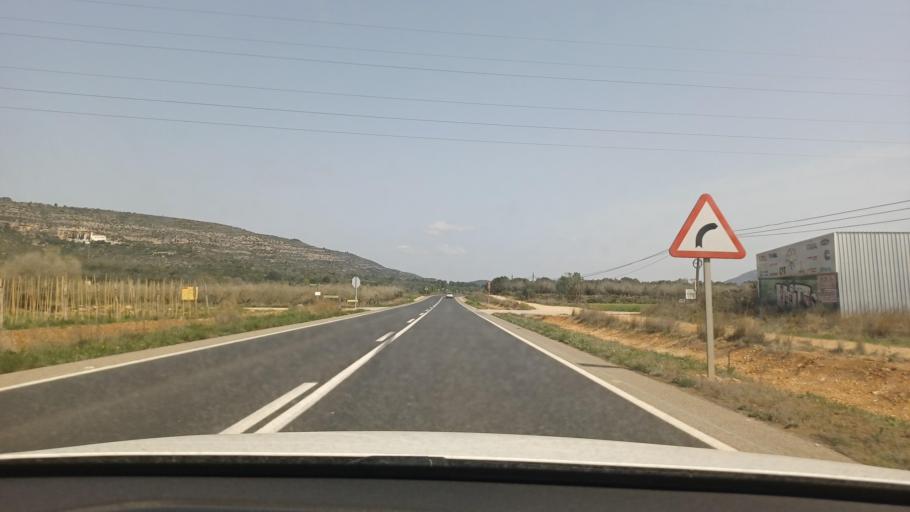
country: ES
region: Catalonia
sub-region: Provincia de Tarragona
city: Ulldecona
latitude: 40.6183
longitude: 0.4686
